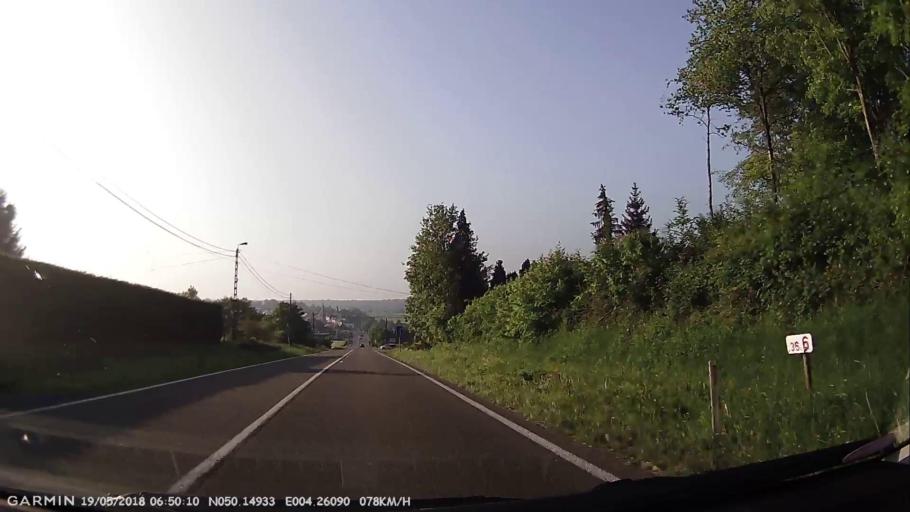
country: BE
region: Wallonia
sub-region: Province du Hainaut
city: Froidchapelle
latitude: 50.1492
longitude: 4.2611
